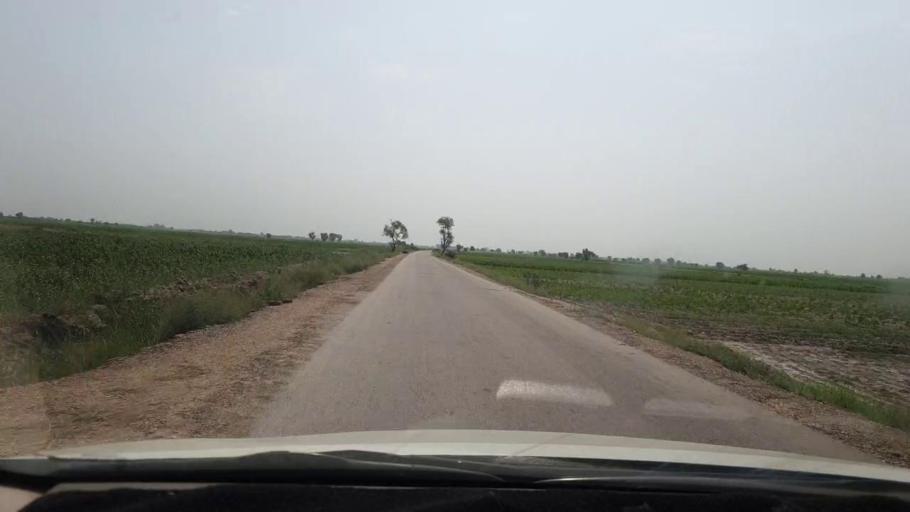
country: PK
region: Sindh
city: Rohri
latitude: 27.5382
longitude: 68.9972
